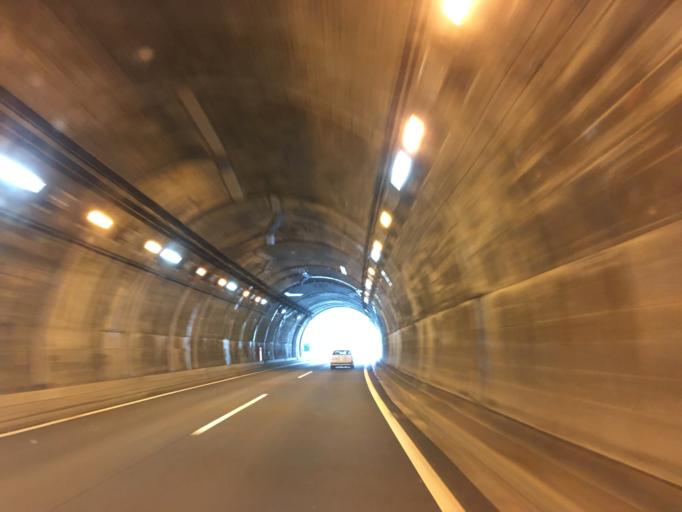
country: JP
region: Yamanashi
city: Uenohara
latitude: 35.6129
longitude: 139.0270
